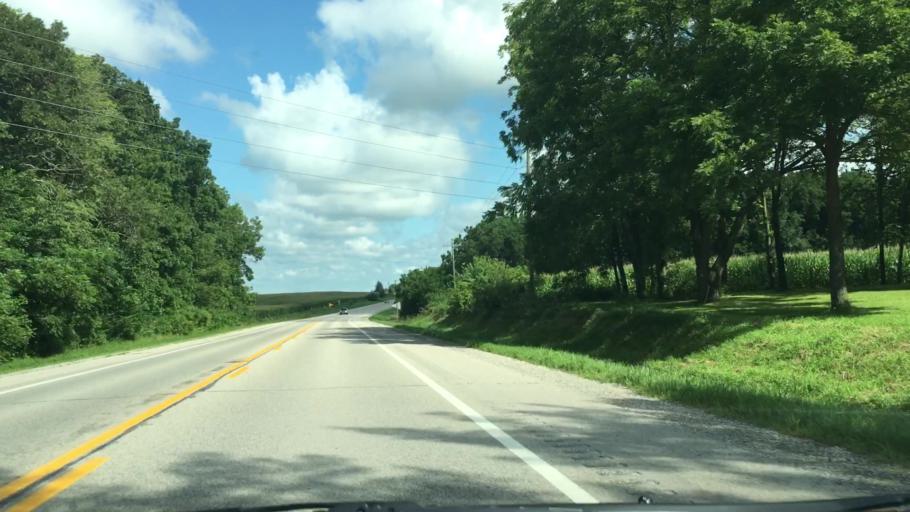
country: US
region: Iowa
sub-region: Johnson County
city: Solon
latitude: 41.7813
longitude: -91.4841
